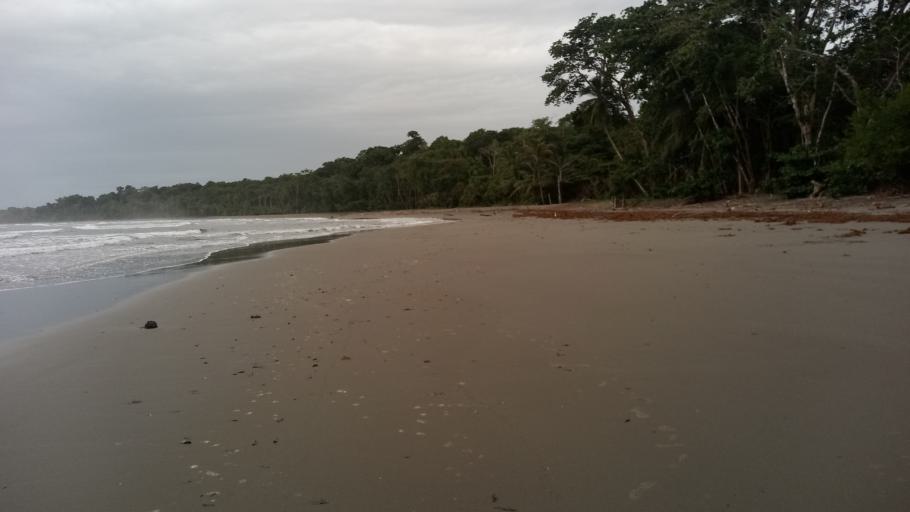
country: CR
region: Limon
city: Sixaola
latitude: 9.6189
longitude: -82.6206
